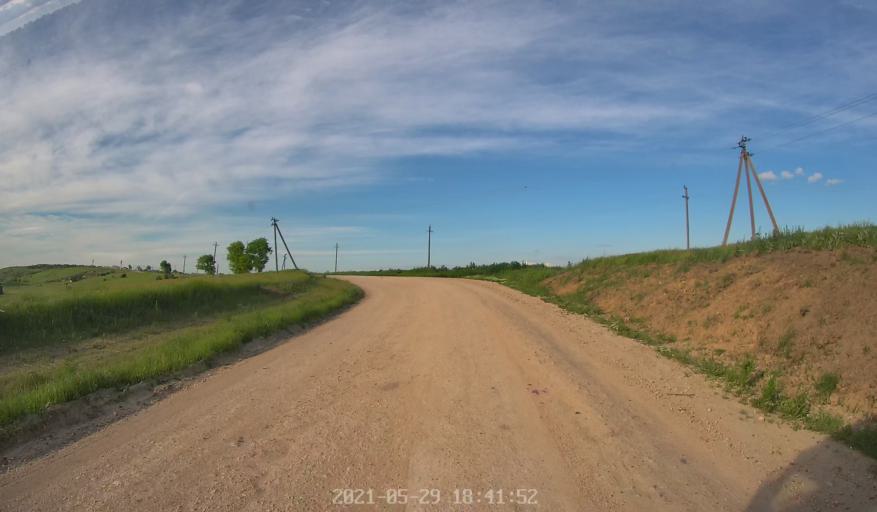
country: MD
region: Chisinau
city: Singera
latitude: 46.8088
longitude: 28.9602
